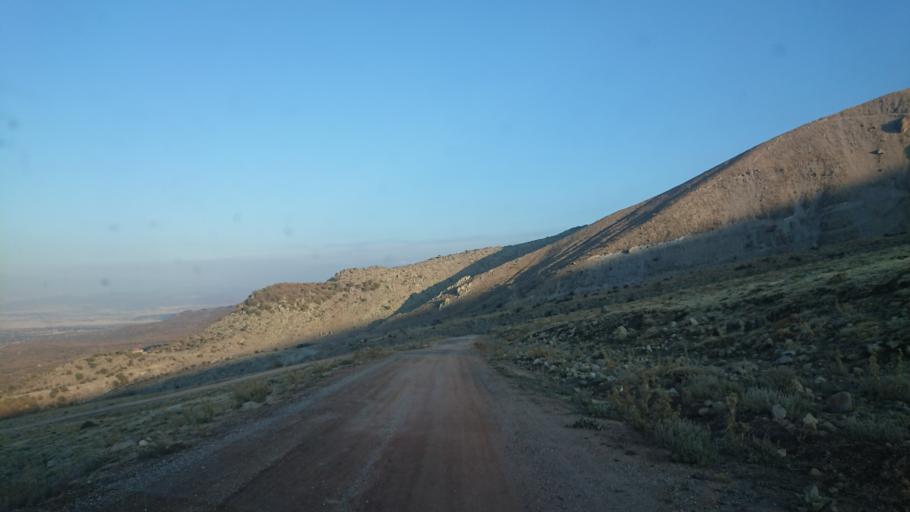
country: TR
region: Aksaray
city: Taspinar
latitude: 38.1611
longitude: 34.1759
